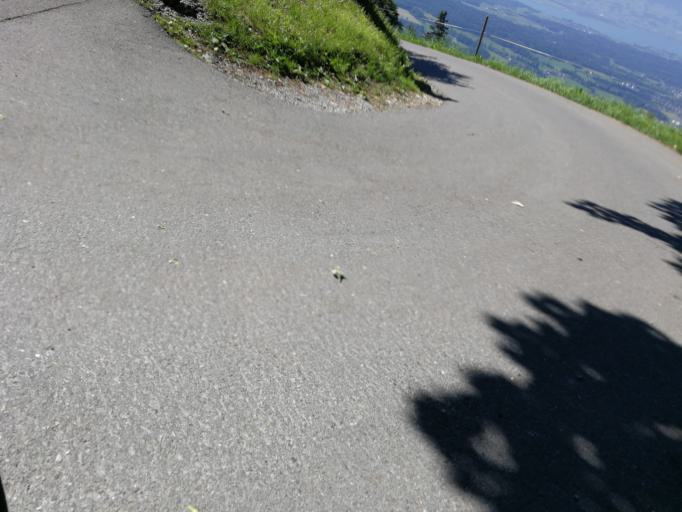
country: CH
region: Zurich
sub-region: Bezirk Hinwil
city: Hadlikon
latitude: 47.2942
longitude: 8.8854
